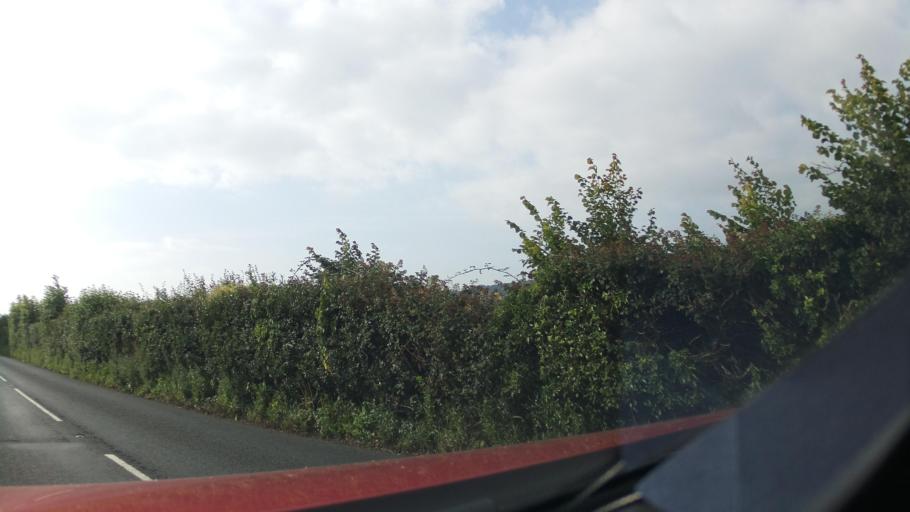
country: GB
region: England
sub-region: North Somerset
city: Long Ashton
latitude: 51.4297
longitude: -2.7047
